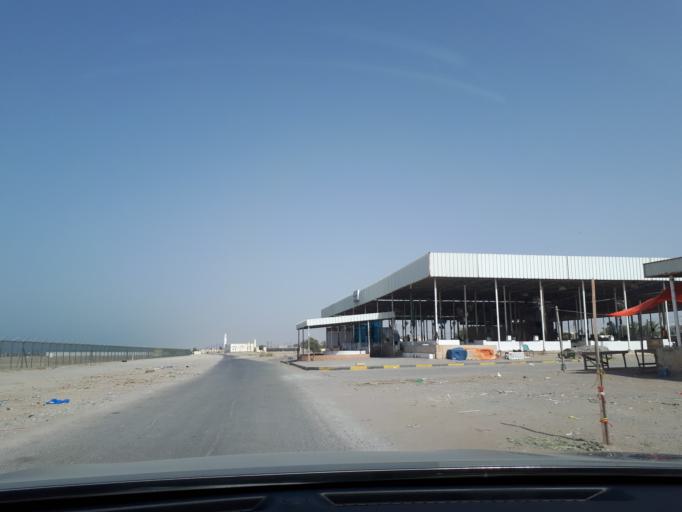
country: OM
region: Al Batinah
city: Barka'
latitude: 23.7097
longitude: 57.8954
